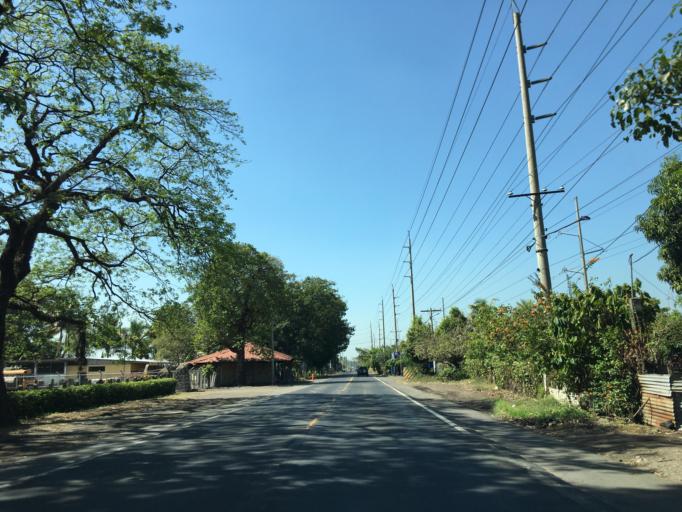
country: GT
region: Escuintla
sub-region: Municipio de Masagua
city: Masagua
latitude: 14.2146
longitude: -90.8360
